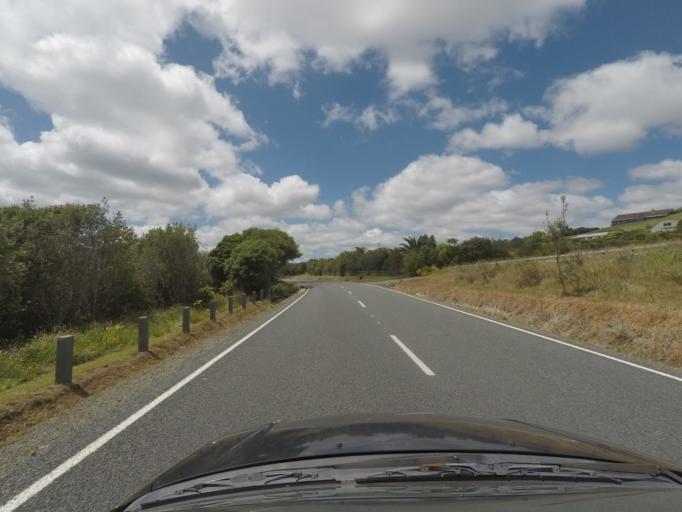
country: NZ
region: Northland
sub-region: Whangarei
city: Ruakaka
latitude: -36.0174
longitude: 174.4907
